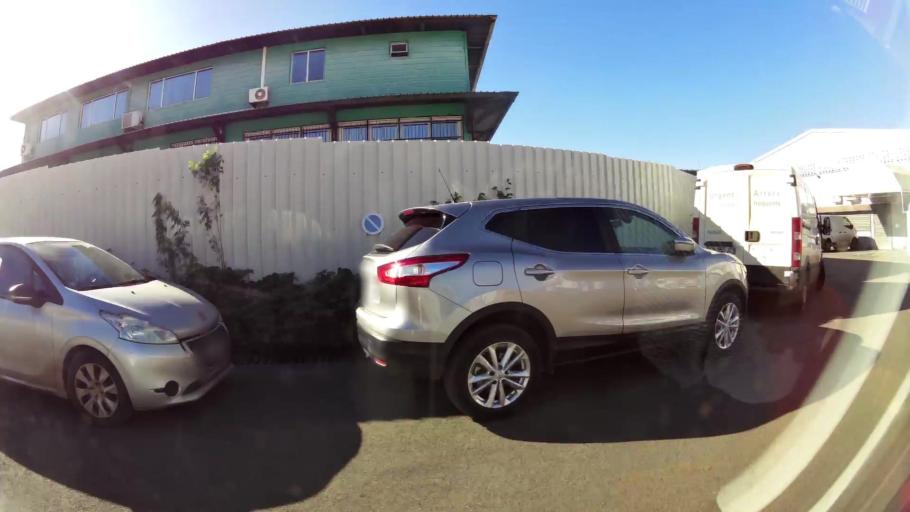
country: YT
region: Mamoudzou
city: Mamoudzou
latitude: -12.7685
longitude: 45.2290
